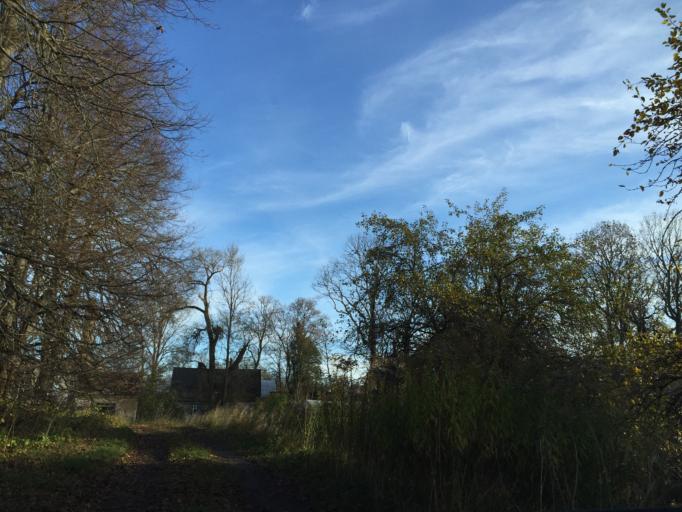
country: LV
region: Skriveri
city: Skriveri
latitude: 56.6241
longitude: 25.1243
